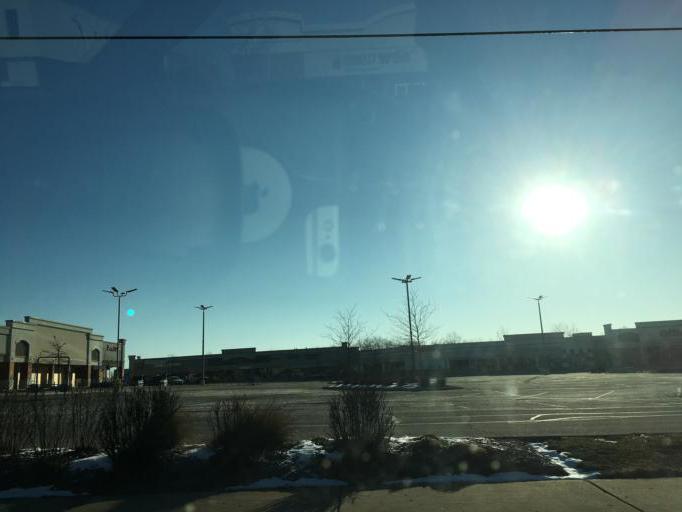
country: US
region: Illinois
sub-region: Cook County
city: Hoffman Estates
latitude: 42.0510
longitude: -88.0796
